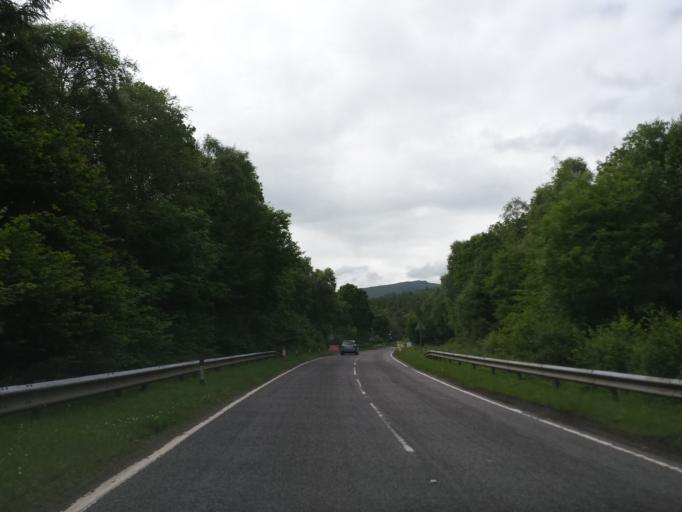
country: GB
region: Scotland
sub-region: Highland
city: Fort William
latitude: 56.8539
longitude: -5.1862
